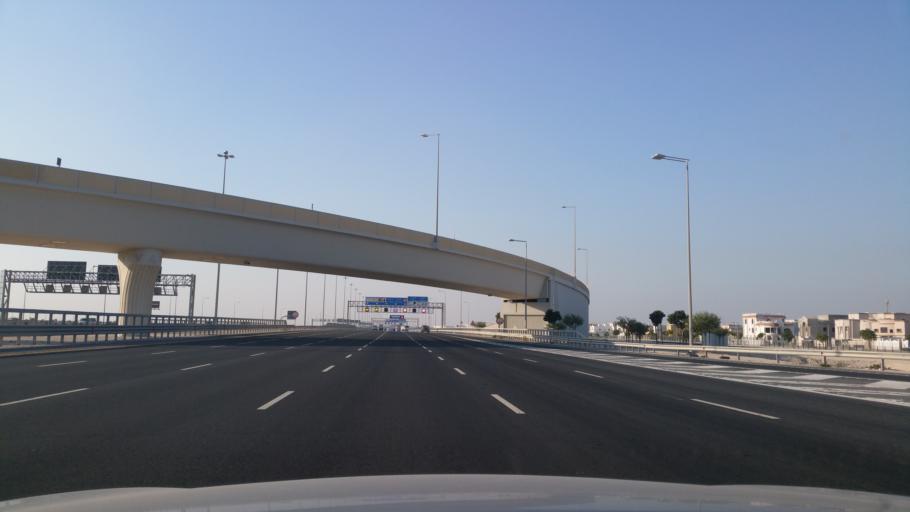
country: QA
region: Al Wakrah
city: Al Wakrah
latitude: 25.1346
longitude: 51.5851
